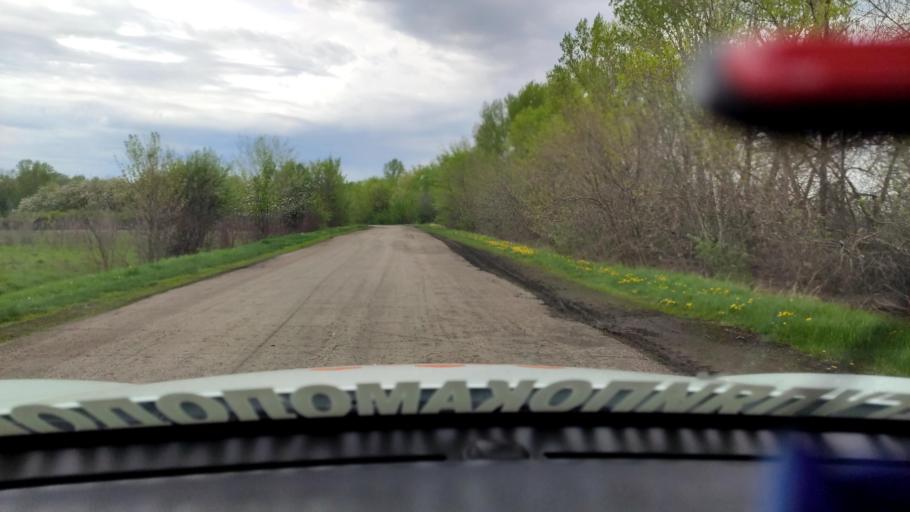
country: RU
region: Voronezj
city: Uryv-Pokrovka
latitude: 51.1183
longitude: 39.1393
